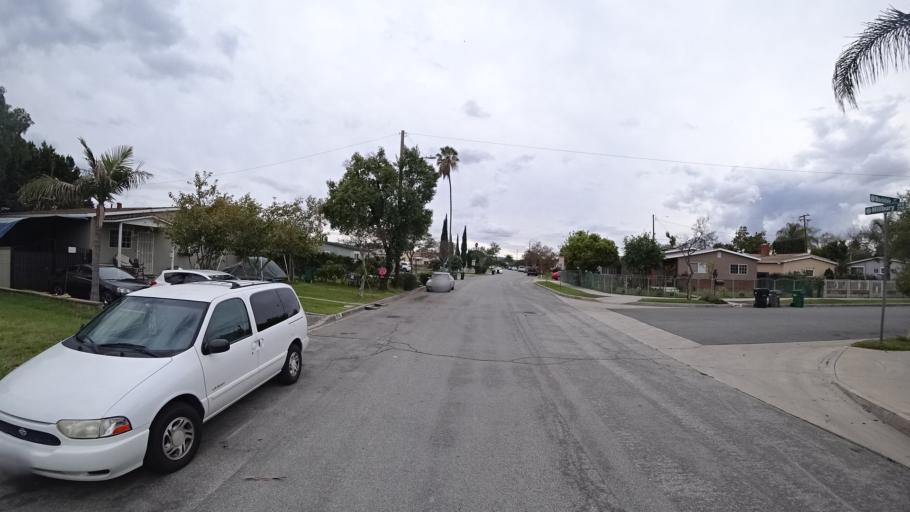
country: US
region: California
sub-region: Los Angeles County
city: Baldwin Park
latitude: 34.0799
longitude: -117.9545
